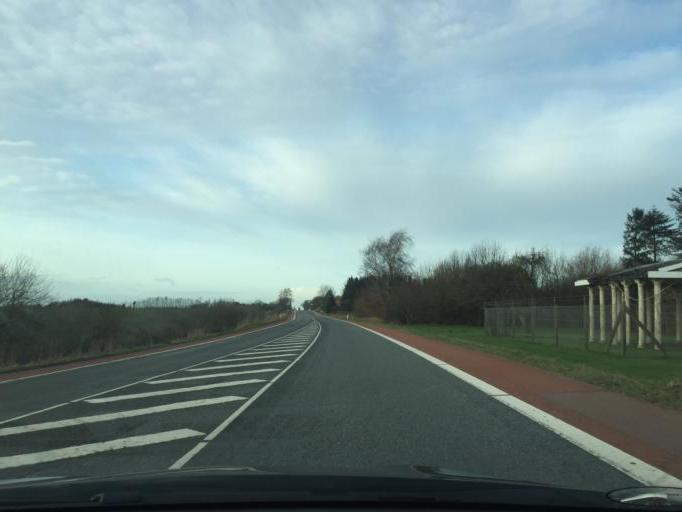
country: DK
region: South Denmark
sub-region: Faaborg-Midtfyn Kommune
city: Ringe
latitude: 55.2625
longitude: 10.4619
